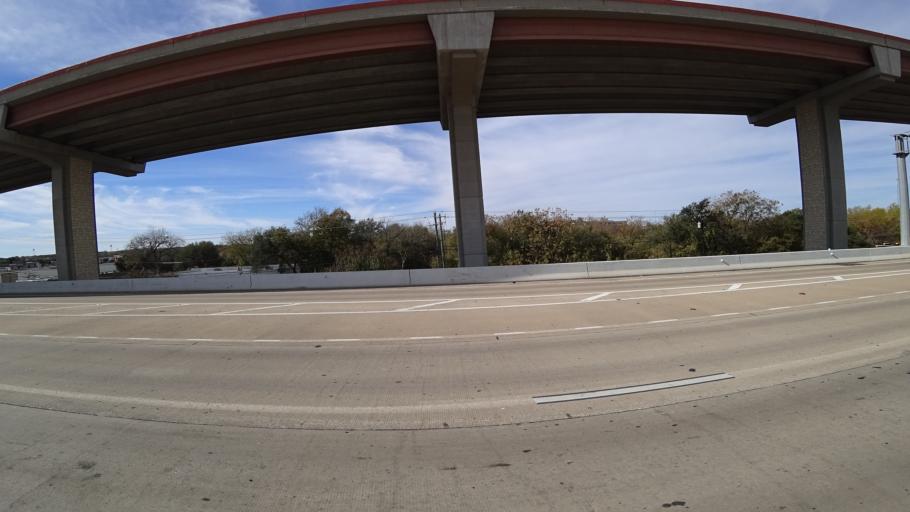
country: US
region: Texas
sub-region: Williamson County
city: Anderson Mill
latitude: 30.4649
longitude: -97.7957
